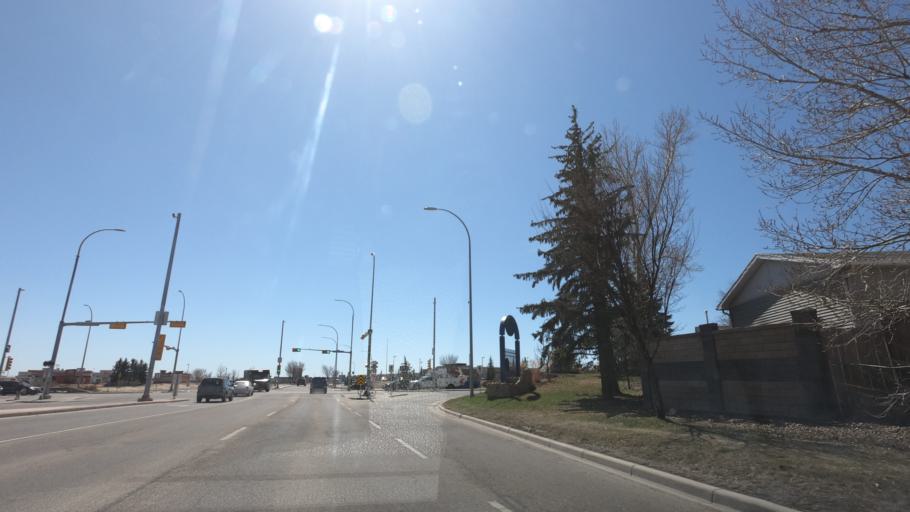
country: CA
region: Alberta
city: Airdrie
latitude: 51.2713
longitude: -114.0082
